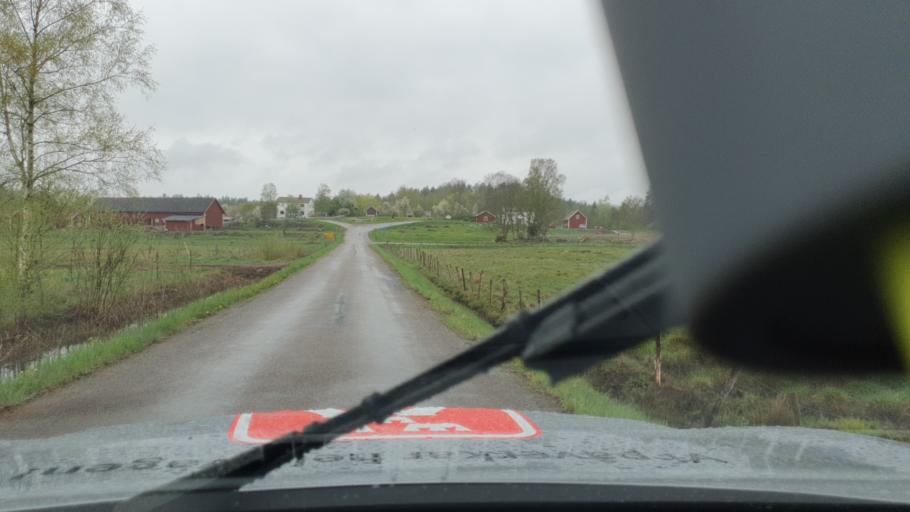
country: SE
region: Kalmar
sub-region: Vimmerby Kommun
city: Vimmerby
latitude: 57.7862
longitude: 16.0165
